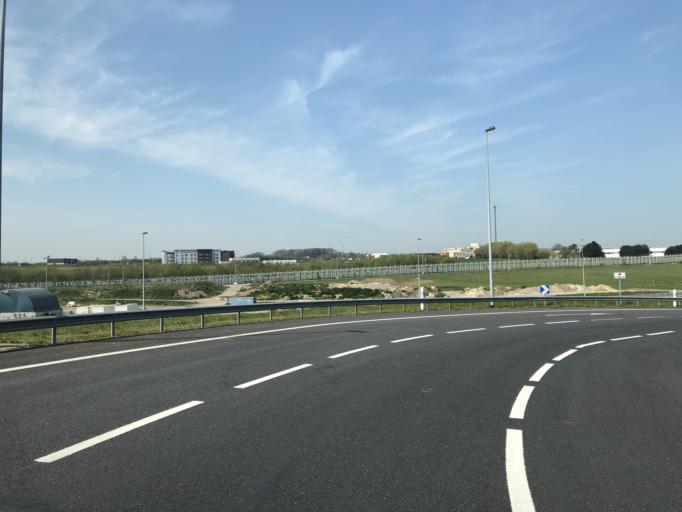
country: FR
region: Nord-Pas-de-Calais
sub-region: Departement du Pas-de-Calais
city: Frethun
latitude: 50.9196
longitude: 1.8088
